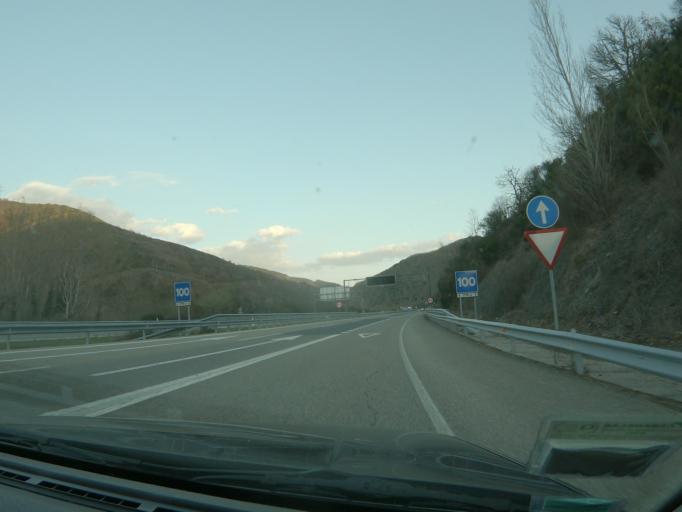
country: ES
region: Castille and Leon
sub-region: Provincia de Leon
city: Trabadelo
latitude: 42.6436
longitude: -6.8740
